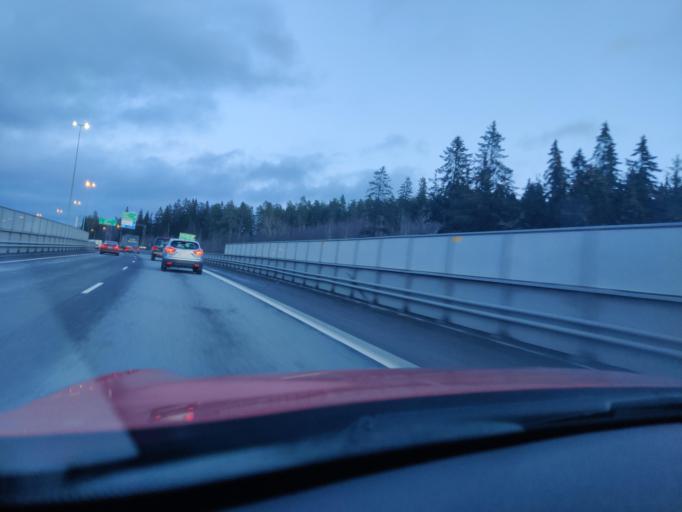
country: FI
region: Pirkanmaa
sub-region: Tampere
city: Tampere
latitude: 61.4599
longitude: 23.7502
